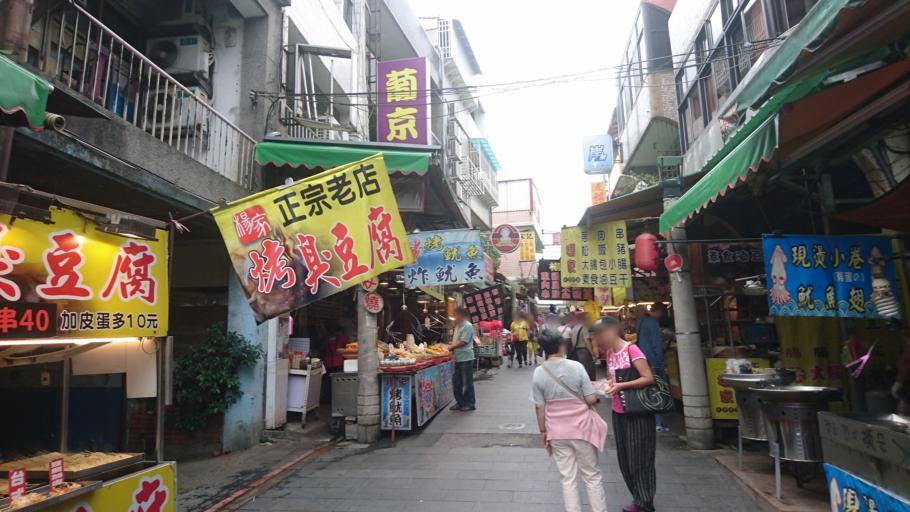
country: TW
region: Taipei
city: Taipei
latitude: 25.1586
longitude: 121.4348
